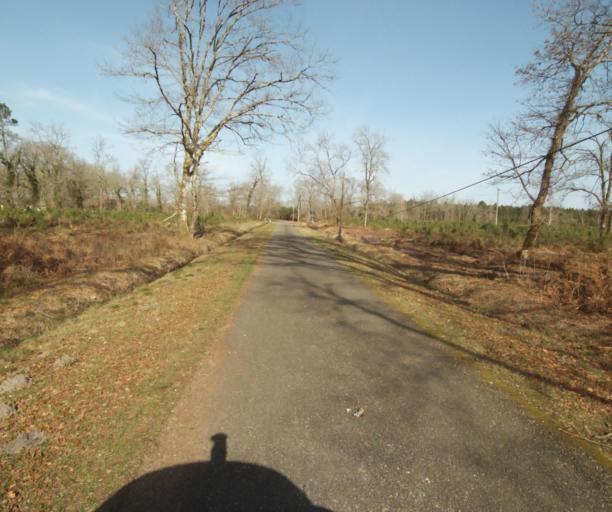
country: FR
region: Aquitaine
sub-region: Departement des Landes
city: Roquefort
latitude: 44.1283
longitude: -0.2124
